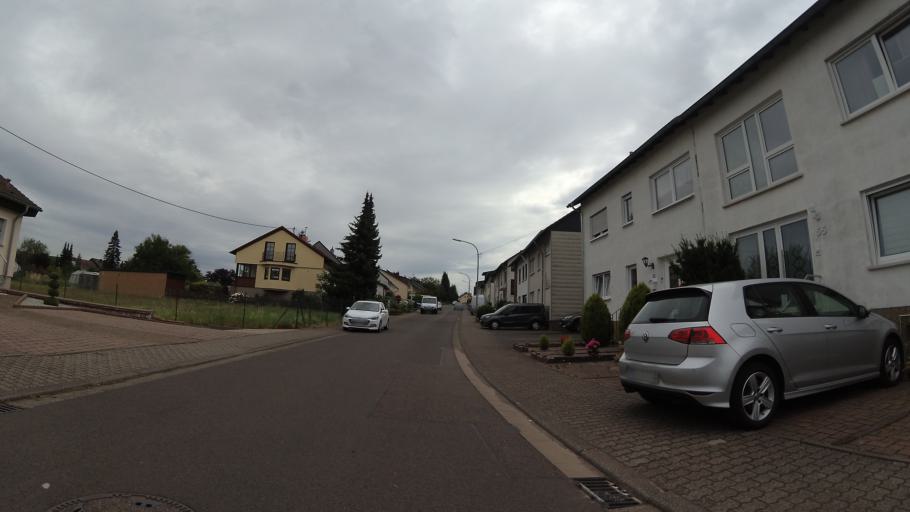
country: DE
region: Saarland
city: Schwalbach
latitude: 49.3147
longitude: 6.8142
